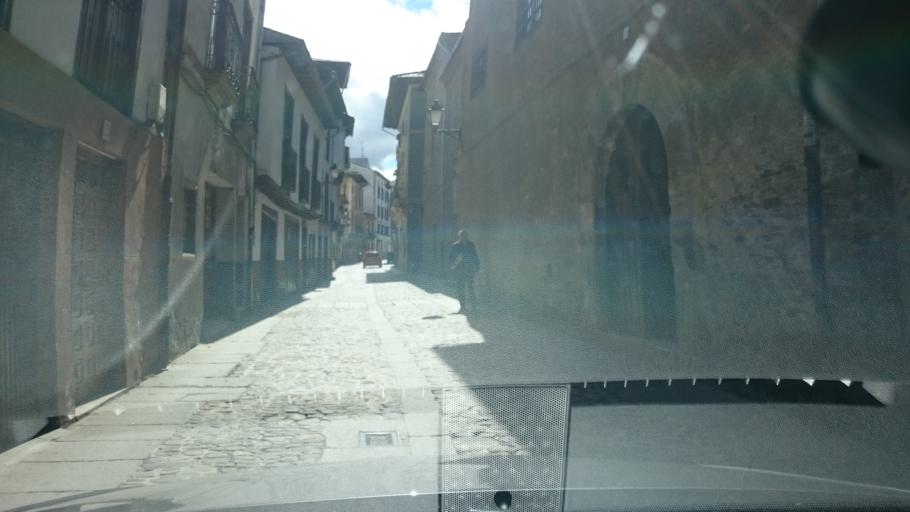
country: ES
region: Castille and Leon
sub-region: Provincia de Leon
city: Villafranca del Bierzo
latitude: 42.6075
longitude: -6.8109
